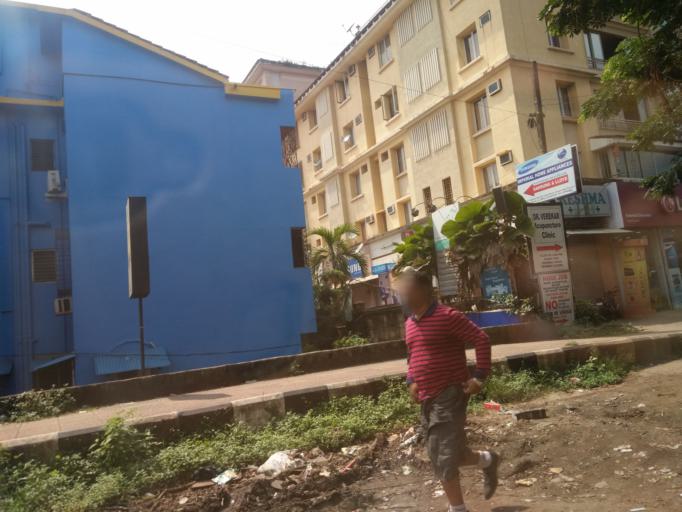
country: IN
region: Goa
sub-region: North Goa
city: Serula
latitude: 15.5349
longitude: 73.8210
